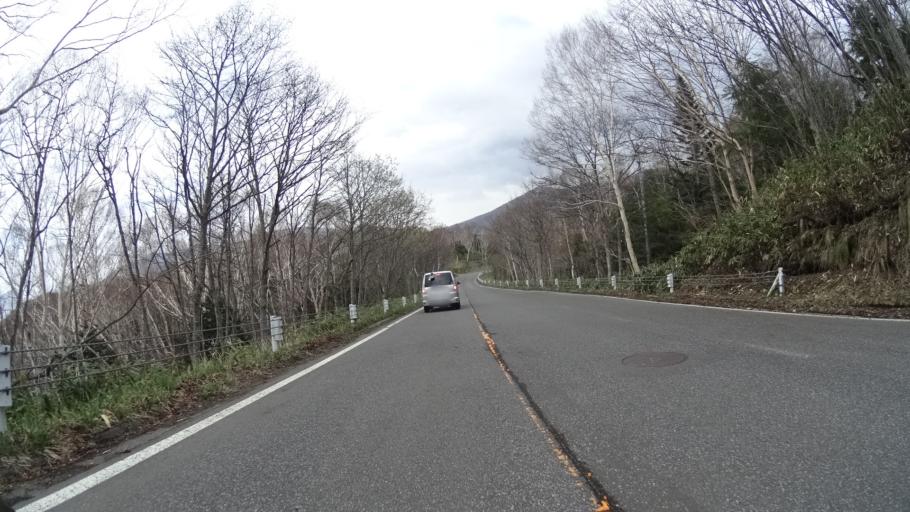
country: JP
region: Nagano
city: Nakano
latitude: 36.7086
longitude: 138.4887
